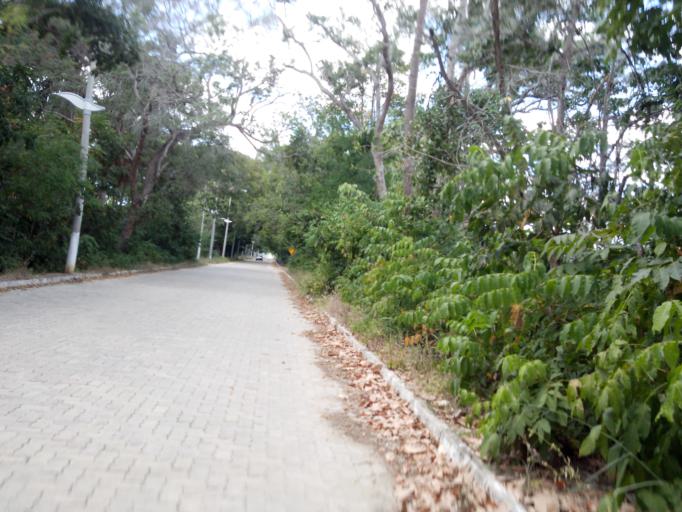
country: BR
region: Ceara
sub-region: Quixada
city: Quixada
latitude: -4.9789
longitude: -39.0609
